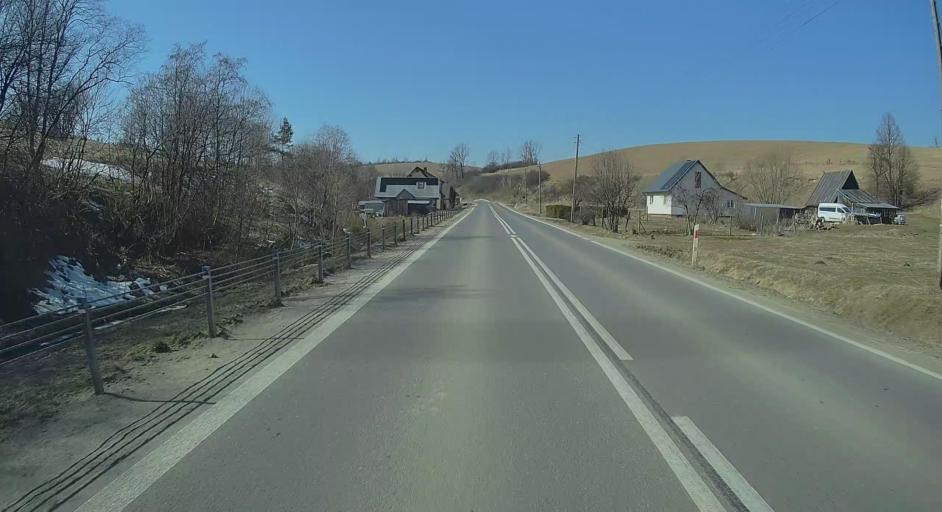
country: PL
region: Subcarpathian Voivodeship
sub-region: Powiat bieszczadzki
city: Ustrzyki Dolne
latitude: 49.4930
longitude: 22.6405
